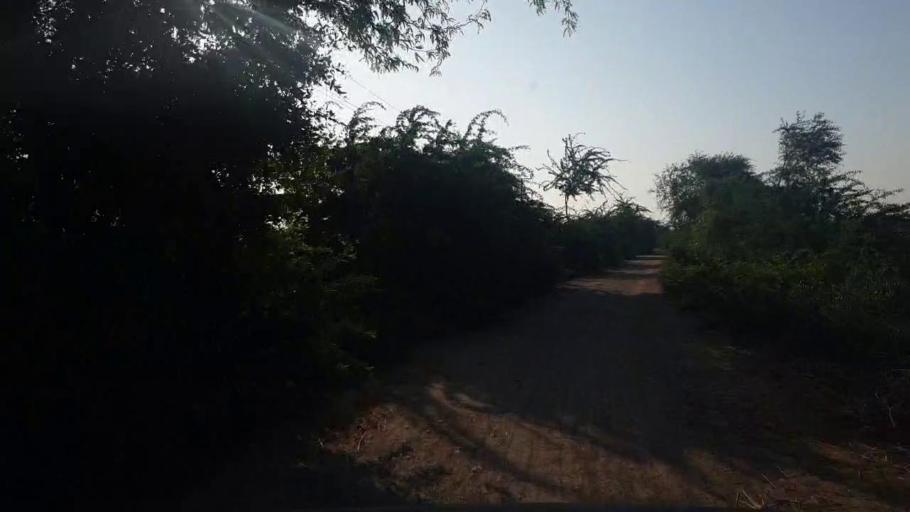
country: PK
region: Sindh
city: Badin
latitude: 24.7342
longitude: 68.8786
